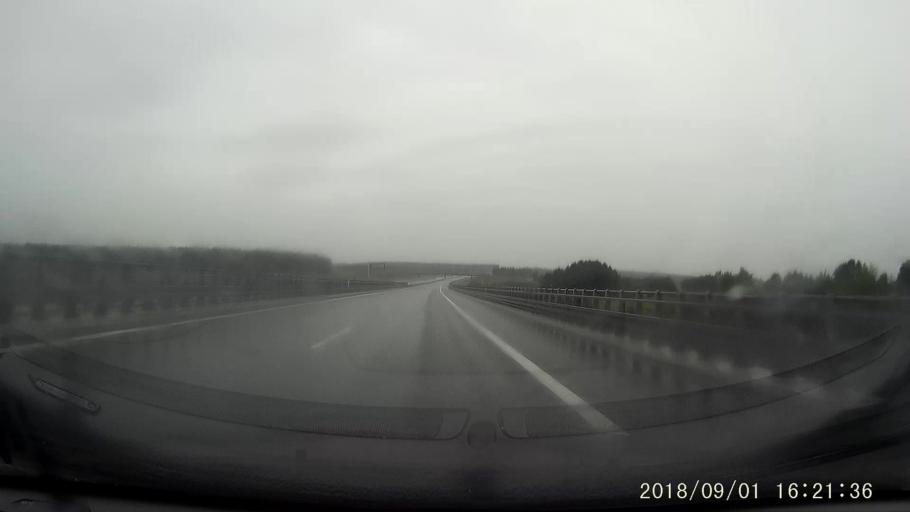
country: PL
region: Lubusz
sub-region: Powiat swiebodzinski
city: Swiebodzin
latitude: 52.3411
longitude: 15.5576
